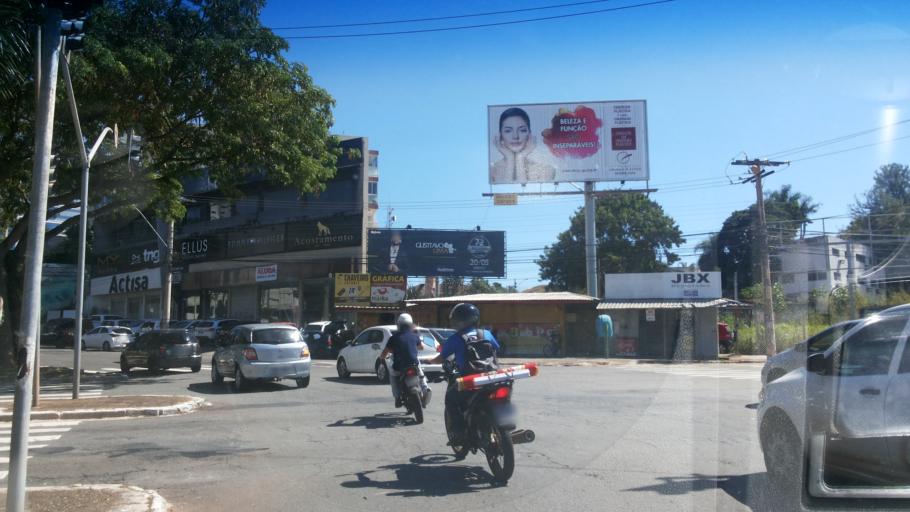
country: BR
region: Goias
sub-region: Goiania
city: Goiania
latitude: -16.6972
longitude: -49.2522
